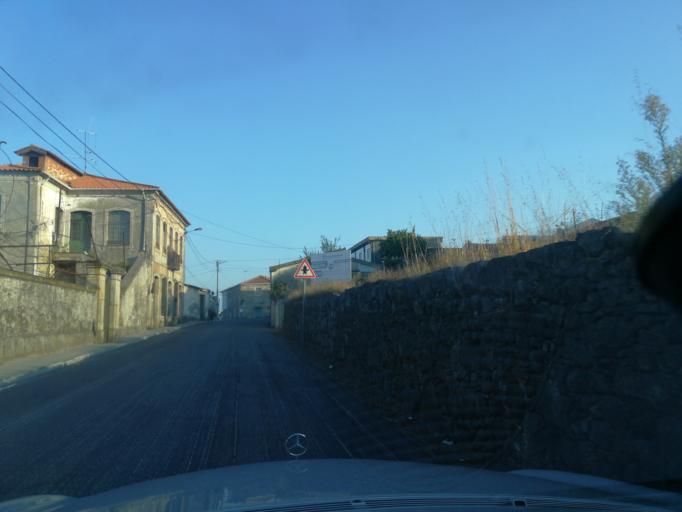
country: PT
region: Braga
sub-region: Braga
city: Braga
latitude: 41.5331
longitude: -8.4299
